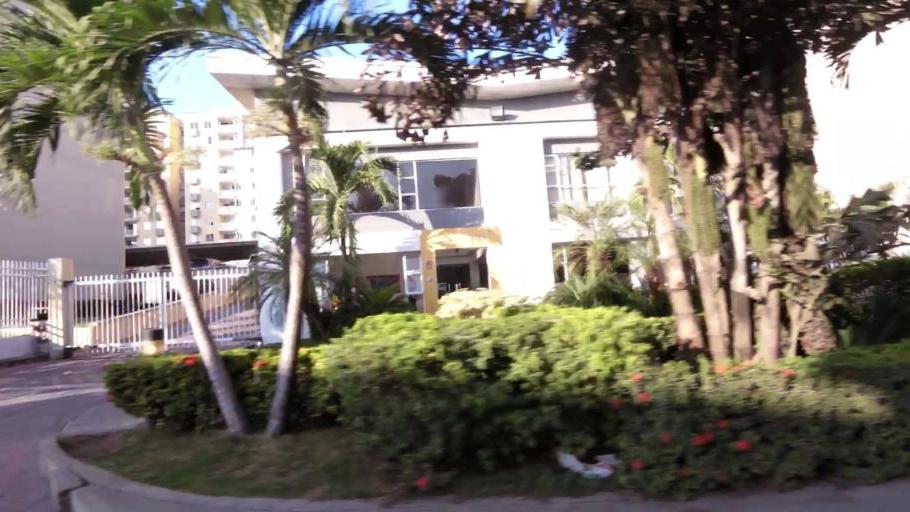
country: CO
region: Bolivar
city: Cartagena
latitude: 10.3876
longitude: -75.4790
